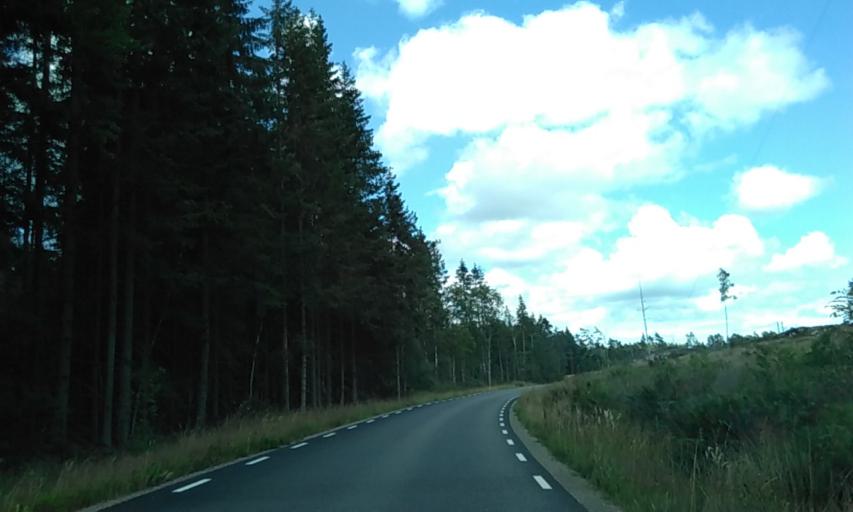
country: SE
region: Vaestra Goetaland
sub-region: Vargarda Kommun
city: Vargarda
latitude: 57.9673
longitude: 12.8741
